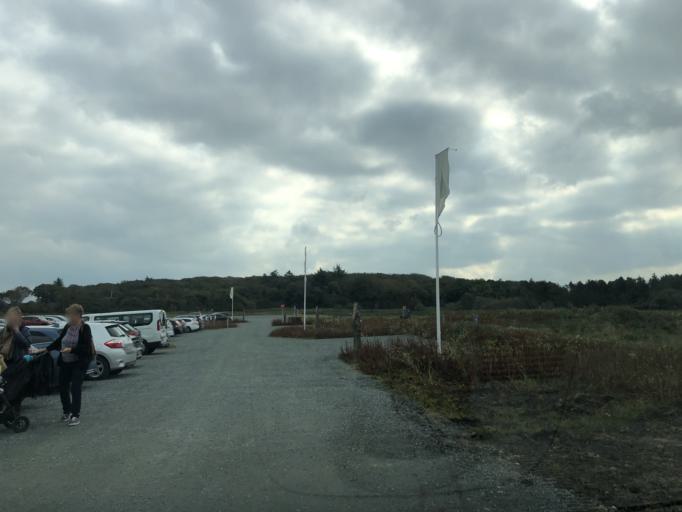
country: DK
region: Central Jutland
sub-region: Ringkobing-Skjern Kommune
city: Ringkobing
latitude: 56.1027
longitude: 8.2460
